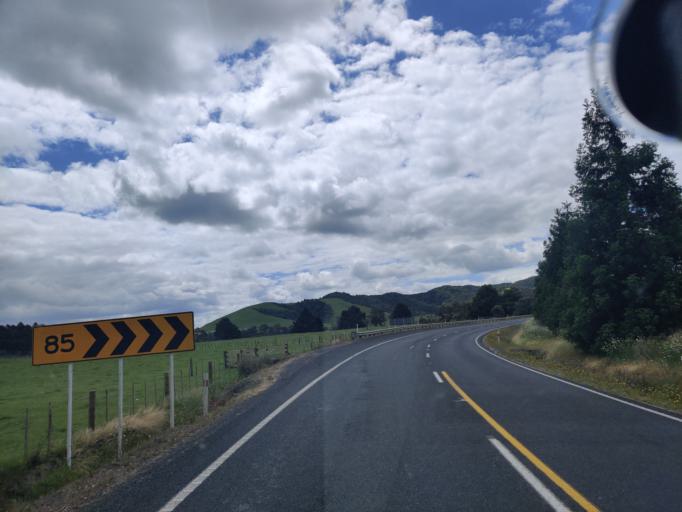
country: NZ
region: Northland
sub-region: Far North District
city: Kerikeri
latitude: -35.2990
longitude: 173.9566
